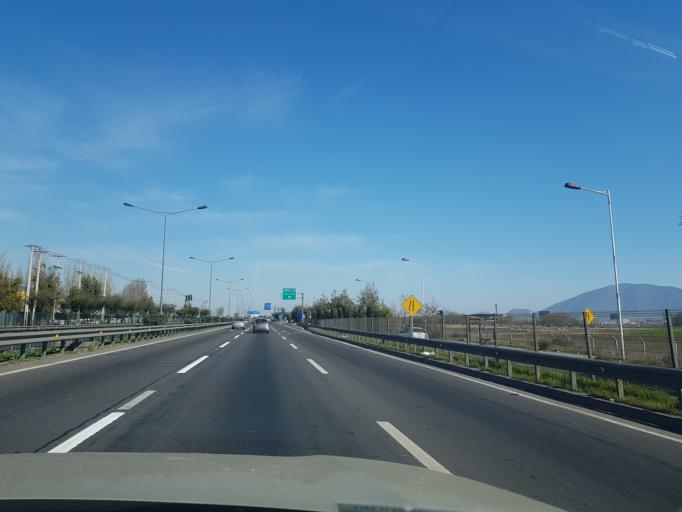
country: CL
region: Santiago Metropolitan
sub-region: Provincia de Santiago
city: Lo Prado
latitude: -33.4084
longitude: -70.7828
